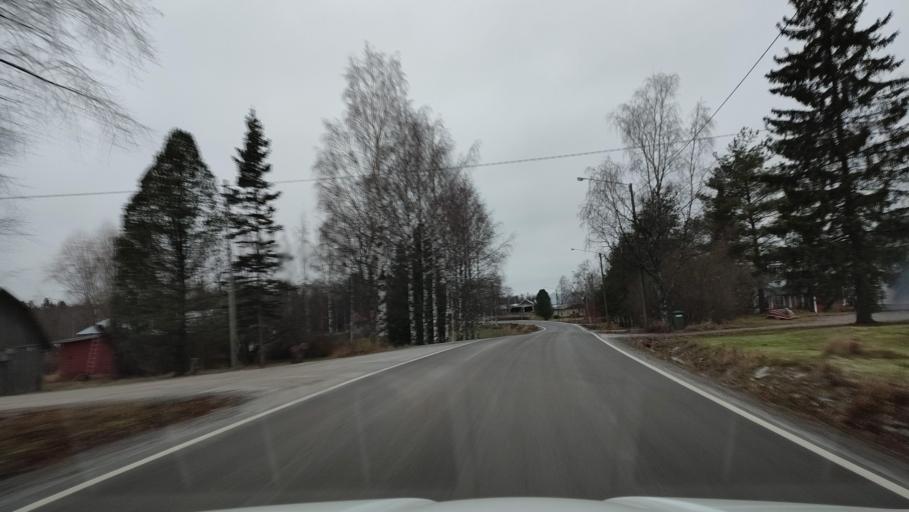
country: FI
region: Ostrobothnia
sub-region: Sydosterbotten
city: Kristinestad
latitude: 62.2485
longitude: 21.5372
